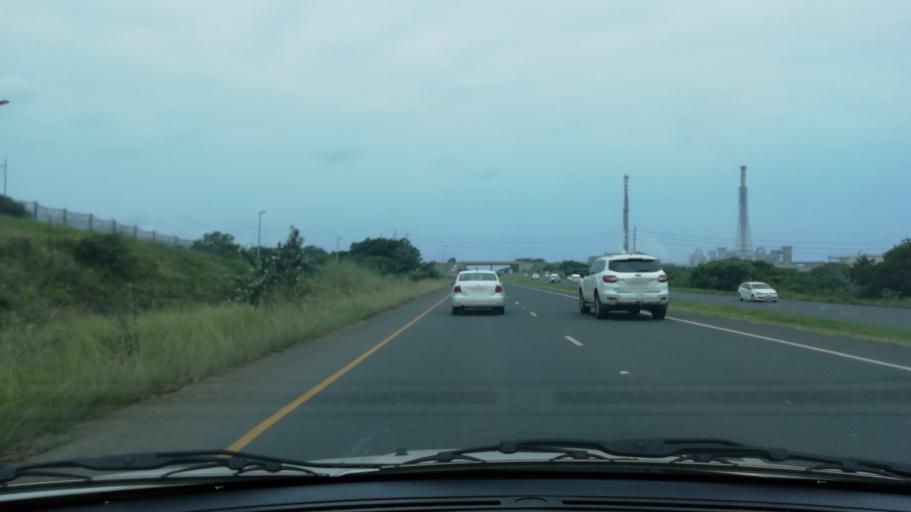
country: ZA
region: KwaZulu-Natal
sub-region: uThungulu District Municipality
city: Richards Bay
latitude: -28.7713
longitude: 32.0289
